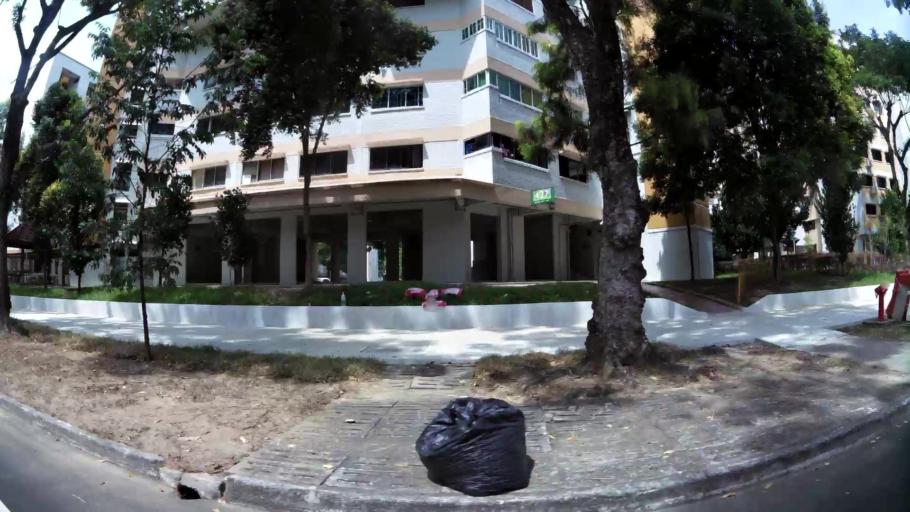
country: MY
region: Johor
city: Johor Bahru
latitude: 1.3512
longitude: 103.7262
